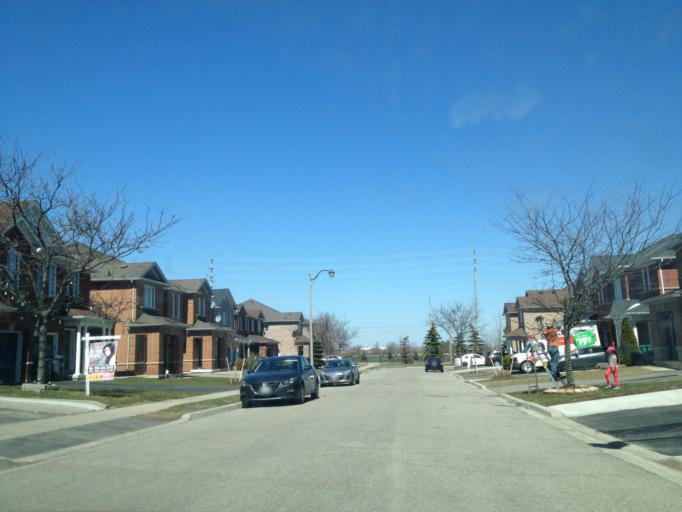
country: CA
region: Ontario
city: Brampton
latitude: 43.6882
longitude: -79.8136
